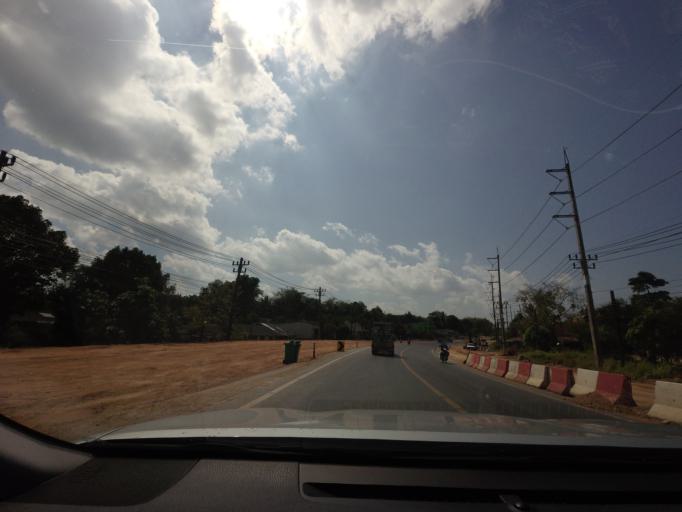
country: TH
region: Phangnga
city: Ban Khao Lak
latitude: 8.7020
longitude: 98.2584
